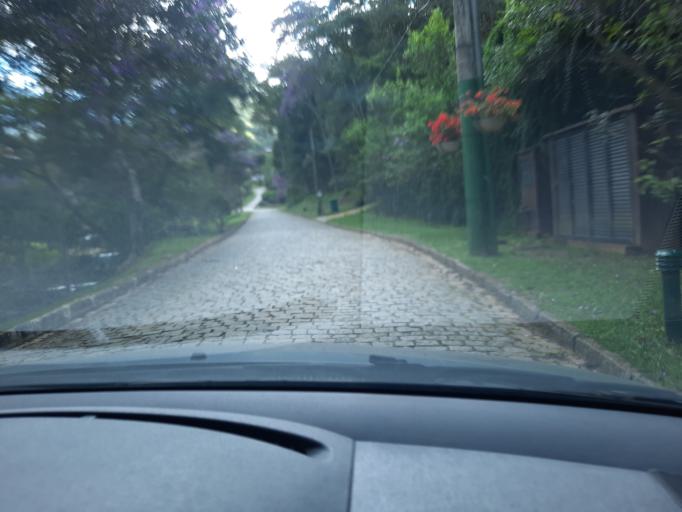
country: BR
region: Rio de Janeiro
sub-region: Petropolis
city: Petropolis
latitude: -22.4396
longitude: -43.1723
